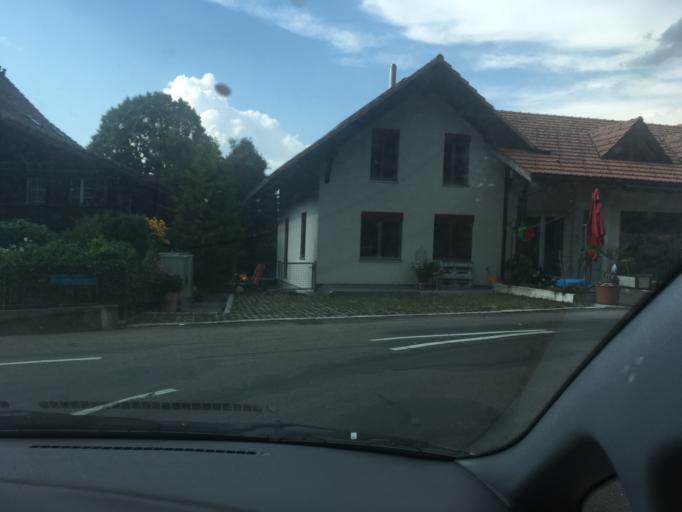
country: CH
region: Bern
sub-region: Bern-Mittelland District
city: Wohlen
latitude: 47.0040
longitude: 7.3367
